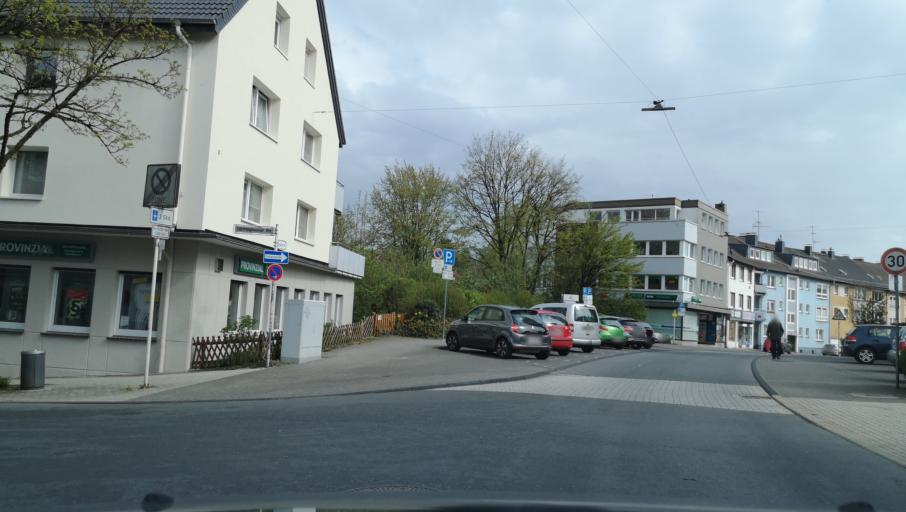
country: DE
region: North Rhine-Westphalia
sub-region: Regierungsbezirk Dusseldorf
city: Remscheid
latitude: 51.2262
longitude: 7.1986
